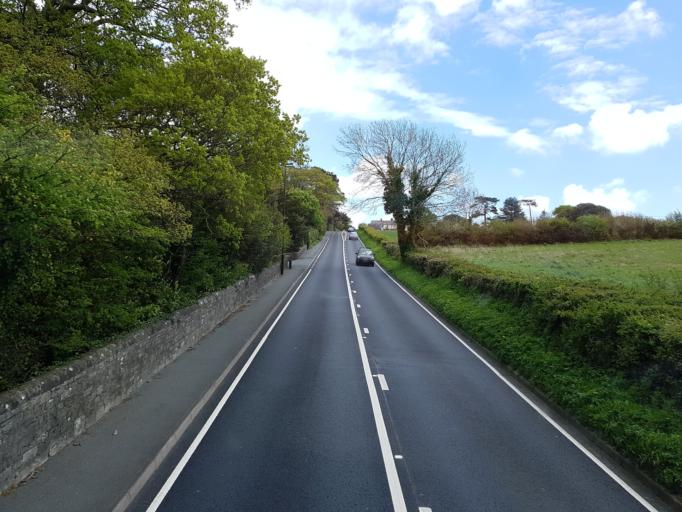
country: GB
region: England
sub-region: Isle of Wight
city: Ryde
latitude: 50.7275
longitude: -1.1959
